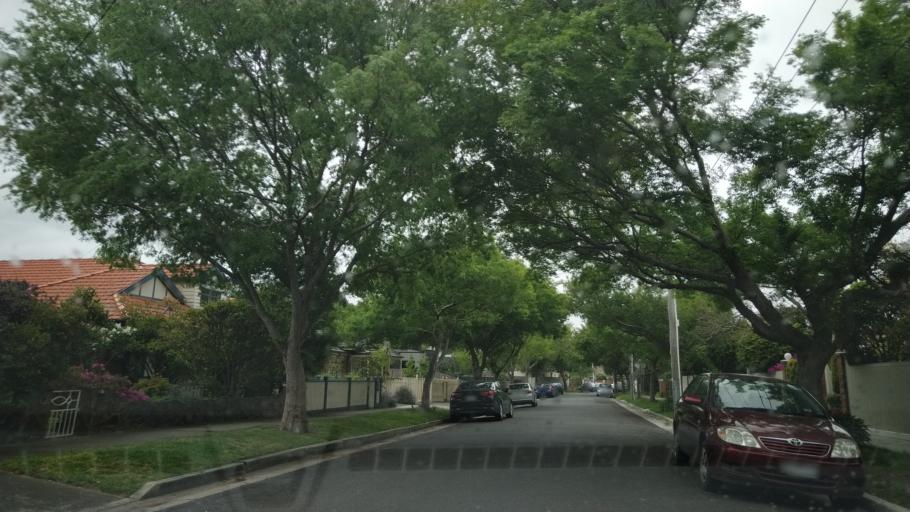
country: AU
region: Victoria
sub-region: Glen Eira
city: Glen Huntly
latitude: -37.8879
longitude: 145.0441
